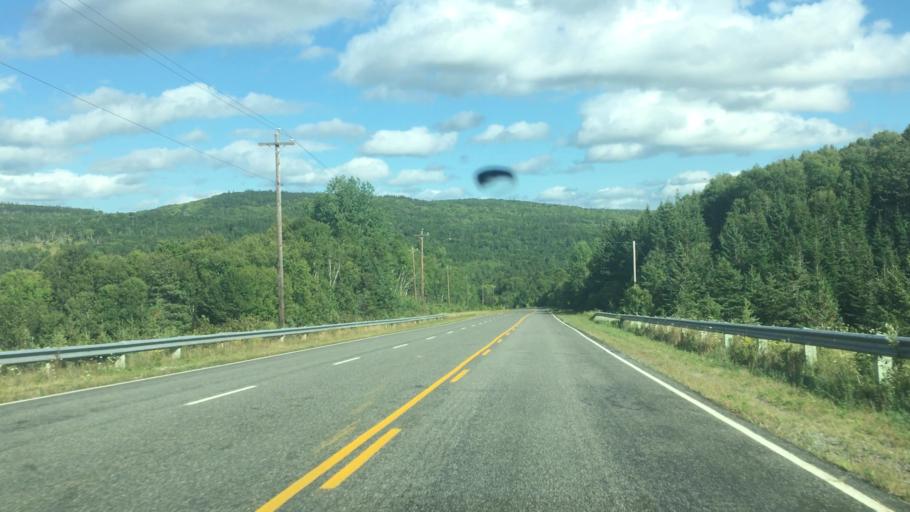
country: CA
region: Nova Scotia
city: Sydney
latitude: 45.8139
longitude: -60.6799
